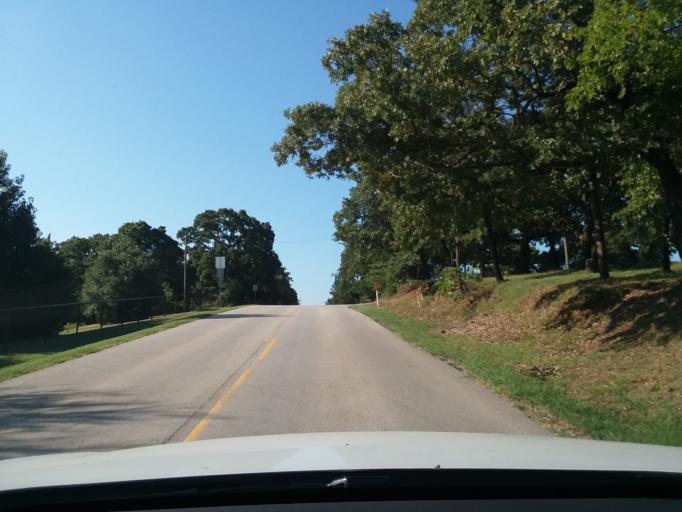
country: US
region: Texas
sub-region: Denton County
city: Bartonville
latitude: 33.0655
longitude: -97.1315
